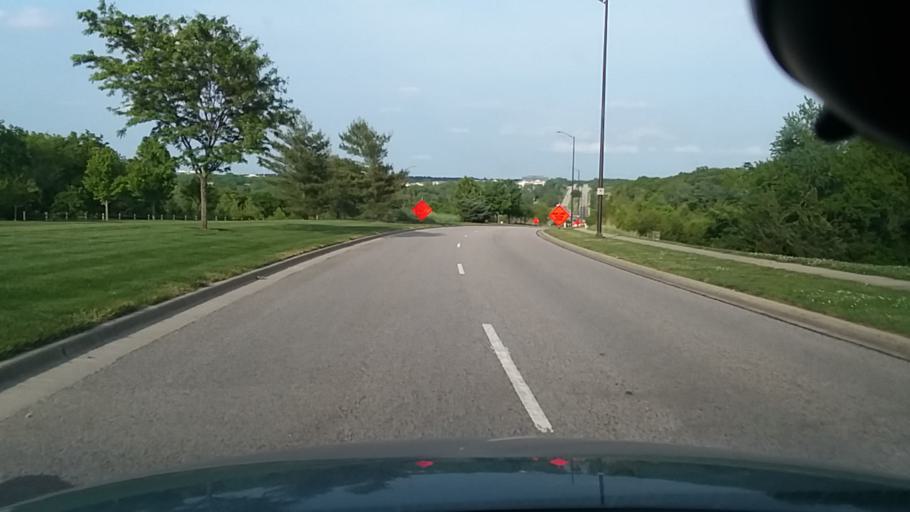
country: US
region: Kansas
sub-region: Johnson County
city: Lenexa
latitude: 38.9557
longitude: -94.8065
